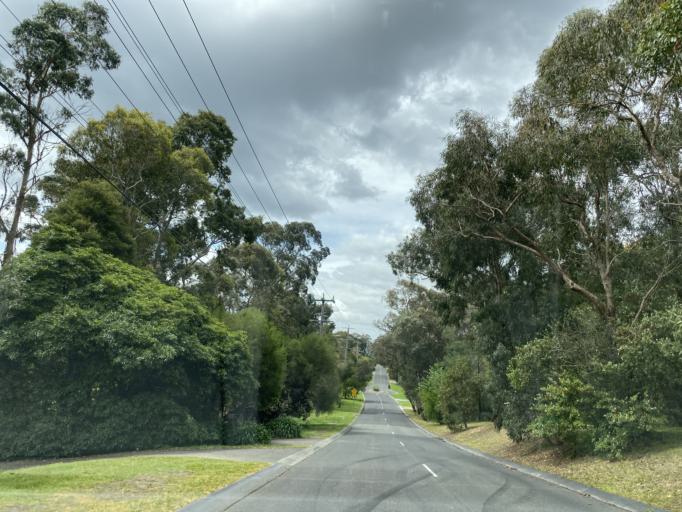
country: AU
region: Victoria
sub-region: Banyule
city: Lower Plenty
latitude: -37.7370
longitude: 145.1261
